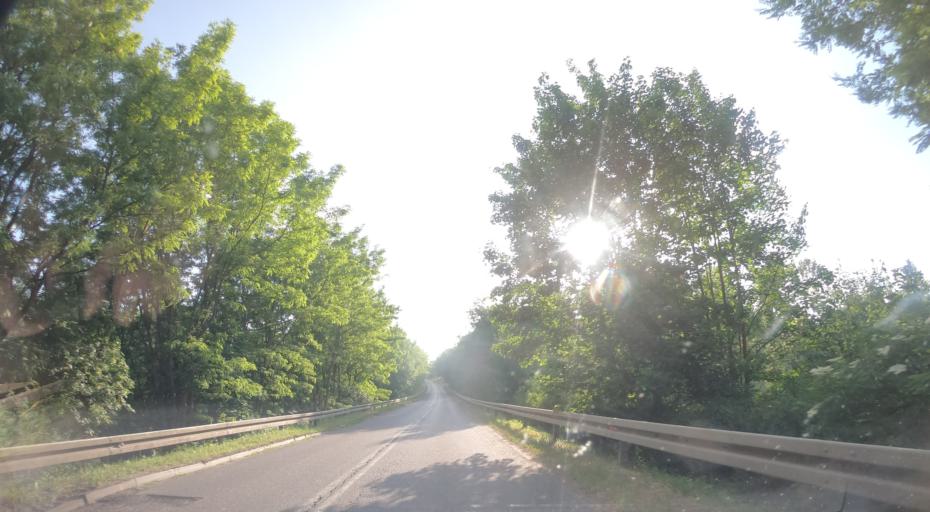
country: PL
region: Lubusz
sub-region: Powiat gorzowski
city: Santok
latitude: 52.7553
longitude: 15.3301
